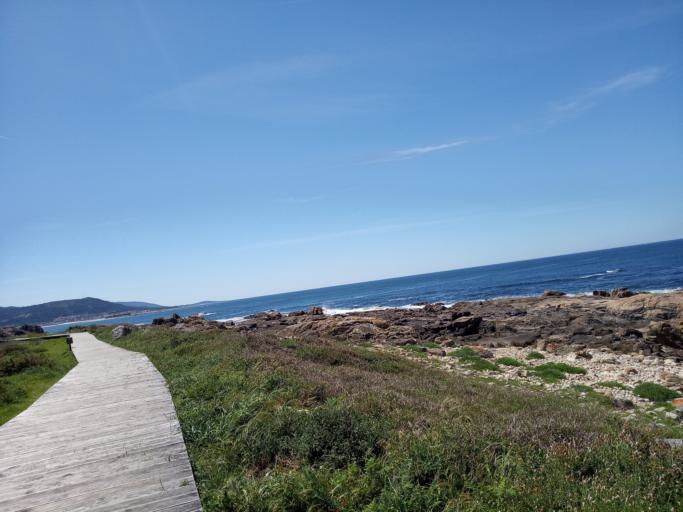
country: ES
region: Galicia
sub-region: Provincia de Pontevedra
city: A Guarda
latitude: 41.8795
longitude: -8.8799
